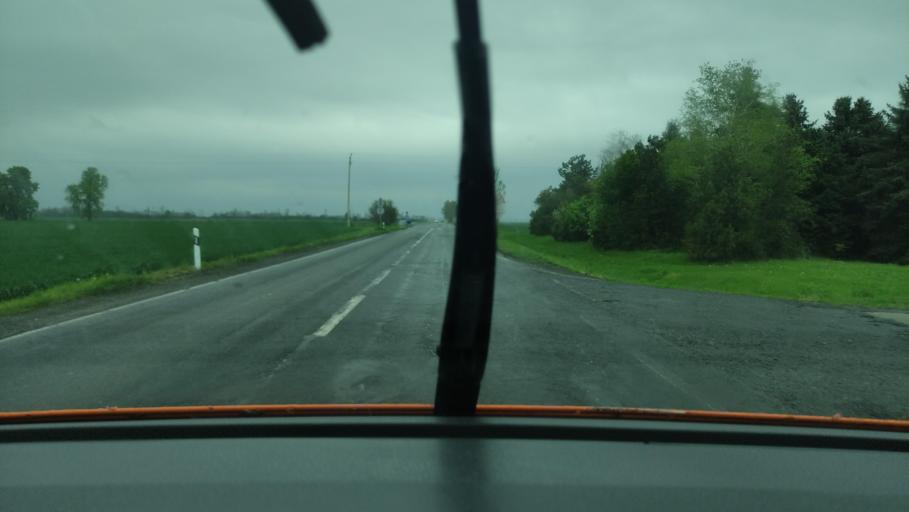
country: HU
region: Baranya
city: Mohacs
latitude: 45.9429
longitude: 18.6644
